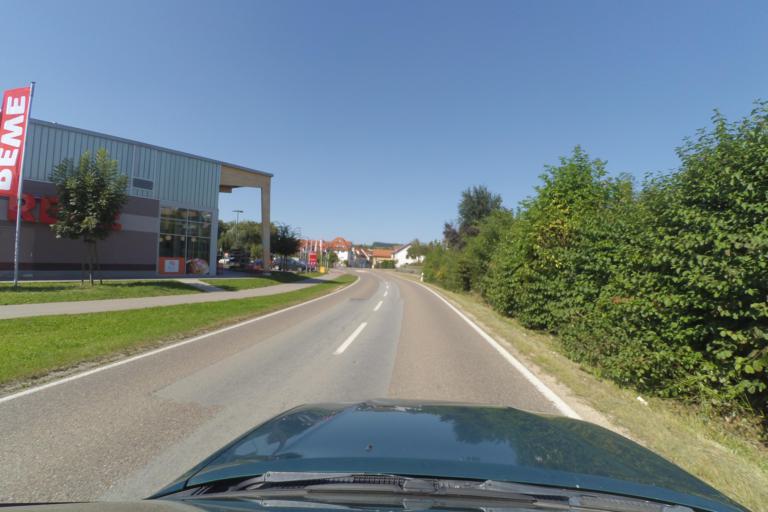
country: DE
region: Baden-Wuerttemberg
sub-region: Regierungsbezirk Stuttgart
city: Bobingen an der Rems
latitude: 48.8173
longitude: 9.9219
